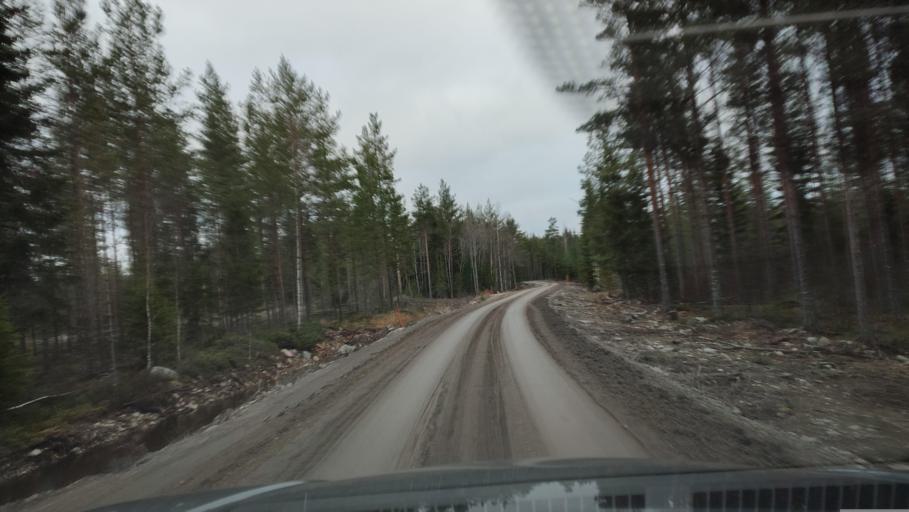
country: FI
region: Southern Ostrobothnia
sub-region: Suupohja
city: Karijoki
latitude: 62.1964
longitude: 21.5892
